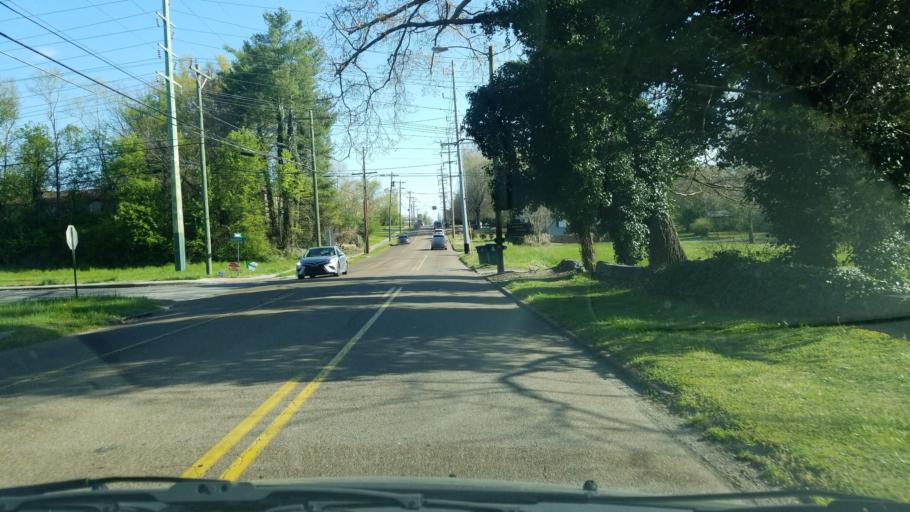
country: US
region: Tennessee
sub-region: Hamilton County
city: East Ridge
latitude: 35.0210
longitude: -85.2481
